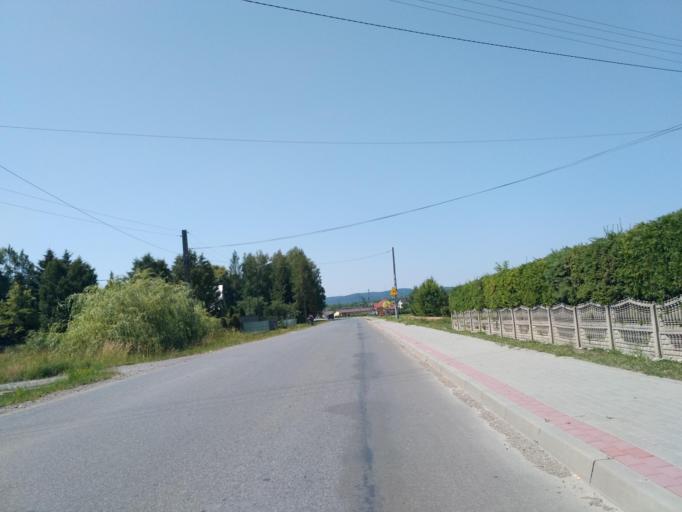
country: PL
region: Subcarpathian Voivodeship
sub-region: Powiat sanocki
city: Niebieszczany
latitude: 49.5482
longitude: 22.1394
